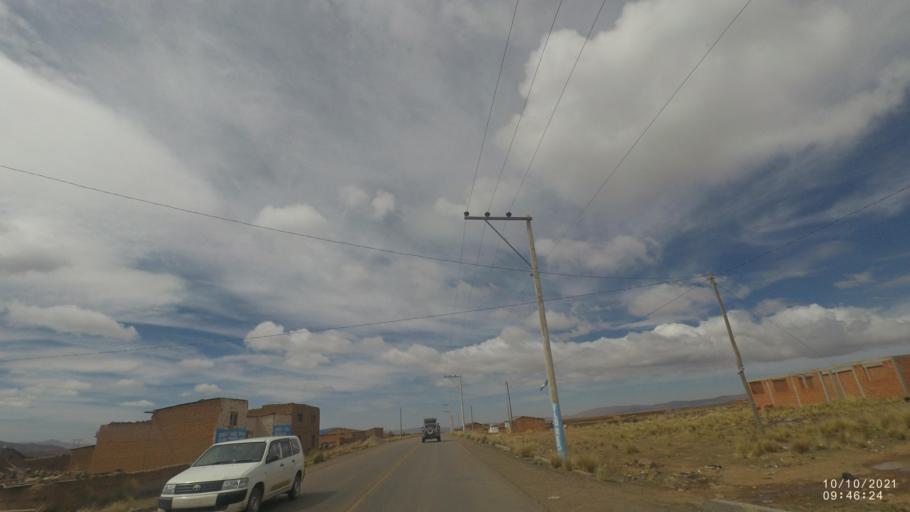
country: BO
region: La Paz
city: Quime
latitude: -17.1797
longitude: -67.3389
